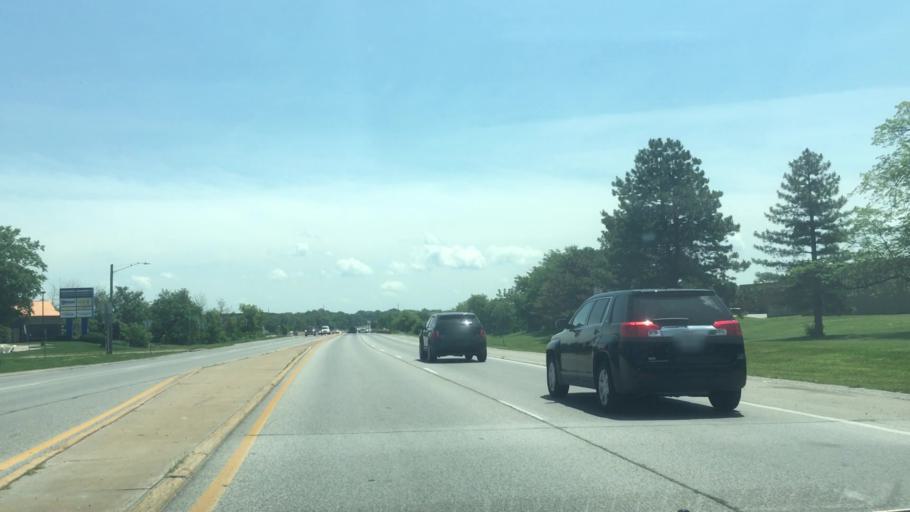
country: US
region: Iowa
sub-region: Johnson County
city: Iowa City
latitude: 41.6471
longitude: -91.5393
